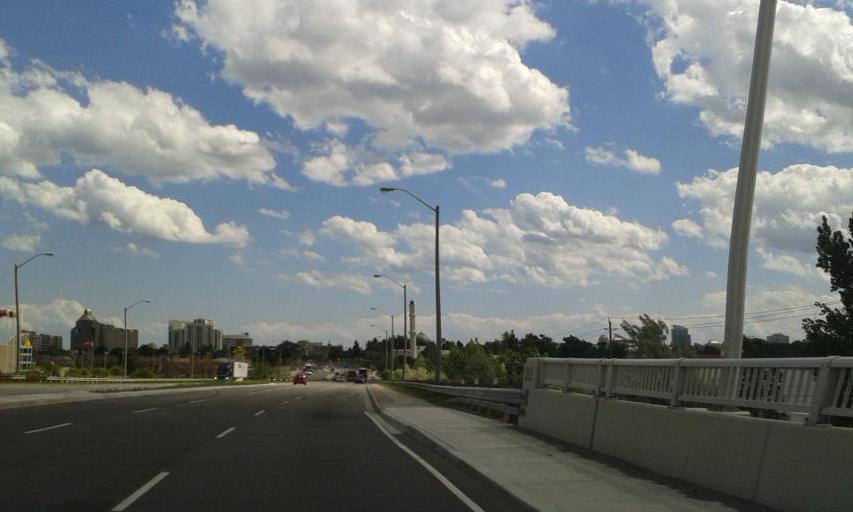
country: CA
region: Ontario
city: Scarborough
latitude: 43.8022
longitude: -79.2422
